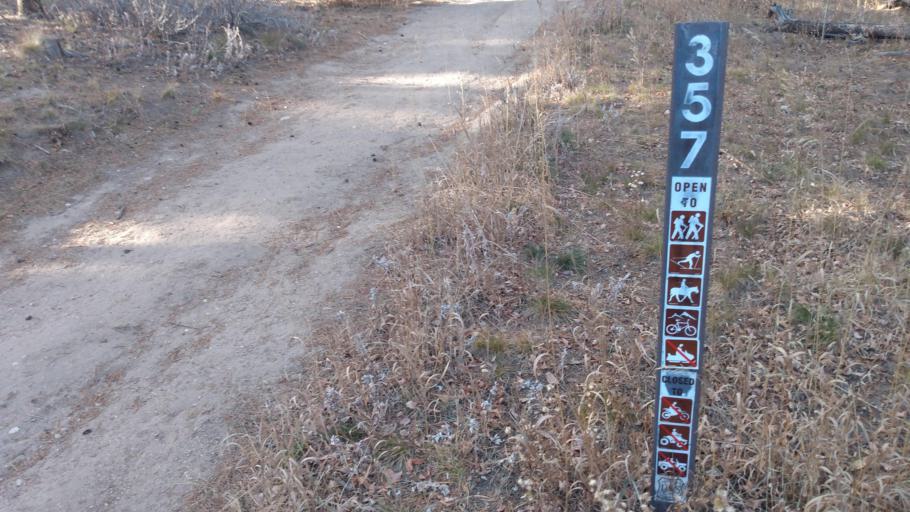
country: US
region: Colorado
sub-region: Boulder County
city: Nederland
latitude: 39.9574
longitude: -105.4474
